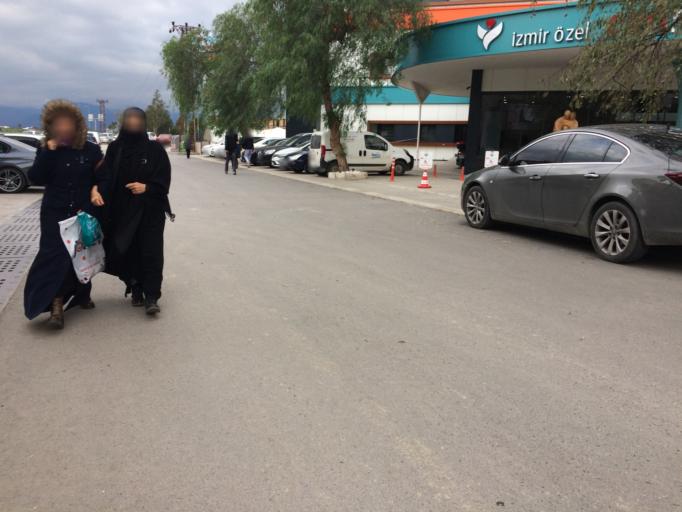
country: TR
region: Izmir
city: Karsiyaka
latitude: 38.4831
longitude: 27.0587
